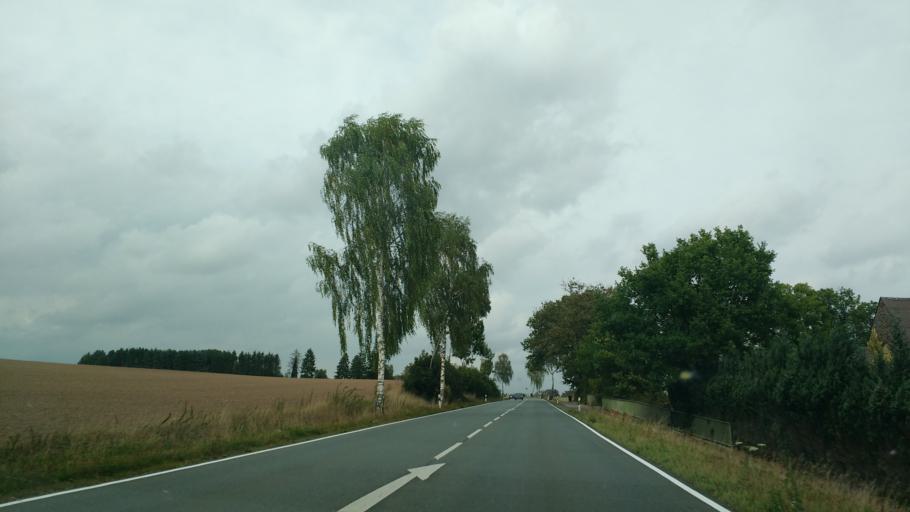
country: DE
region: North Rhine-Westphalia
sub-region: Regierungsbezirk Detmold
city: Detmold
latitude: 51.9753
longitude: 8.8960
